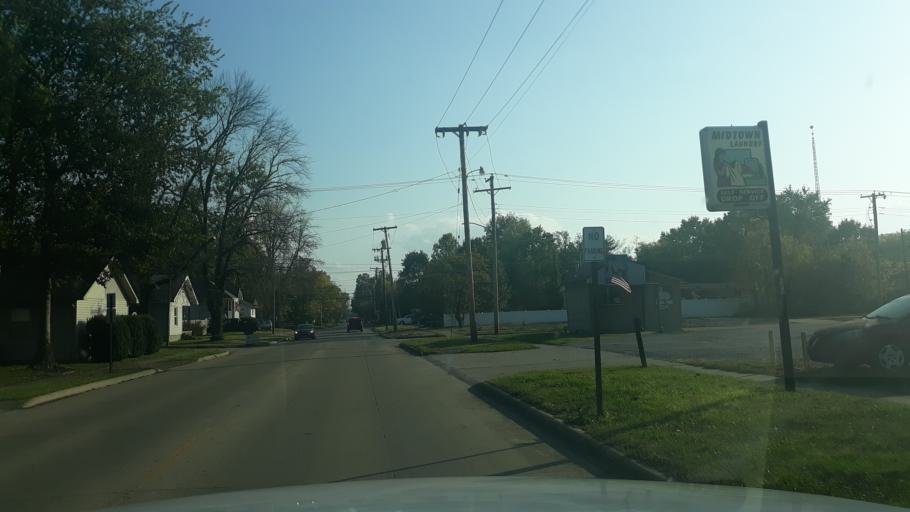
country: US
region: Illinois
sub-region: Saline County
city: Harrisburg
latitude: 37.7324
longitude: -88.5403
